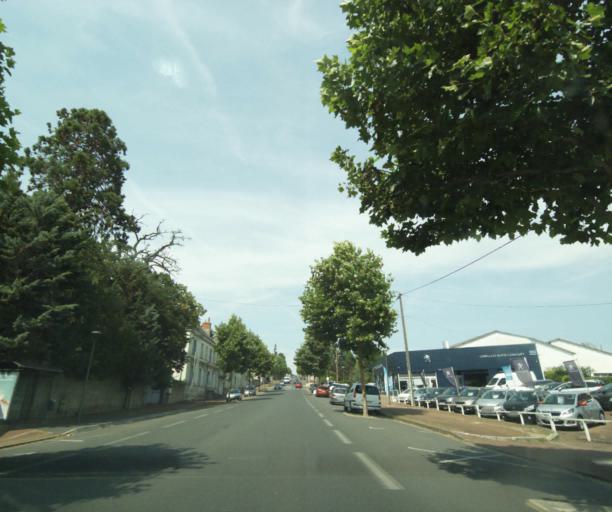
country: FR
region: Centre
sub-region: Departement d'Indre-et-Loire
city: Sainte-Maure-de-Touraine
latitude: 47.1132
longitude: 0.6172
